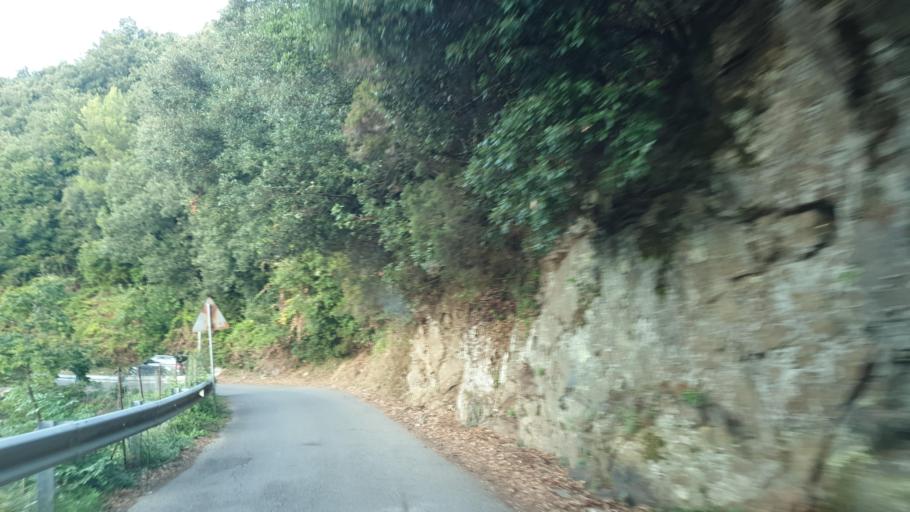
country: IT
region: Liguria
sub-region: Provincia di La Spezia
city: Bonassola
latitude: 44.1898
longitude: 9.5855
